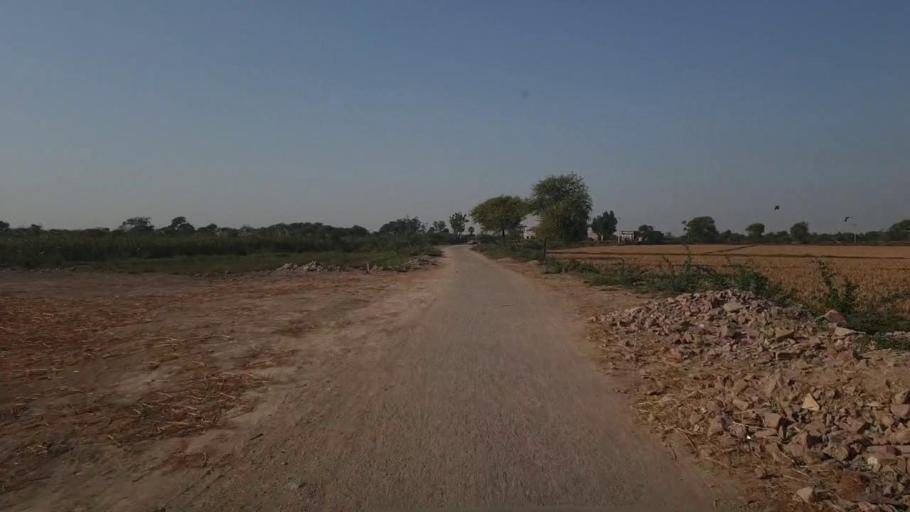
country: PK
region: Sindh
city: Badin
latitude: 24.6550
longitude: 68.8119
